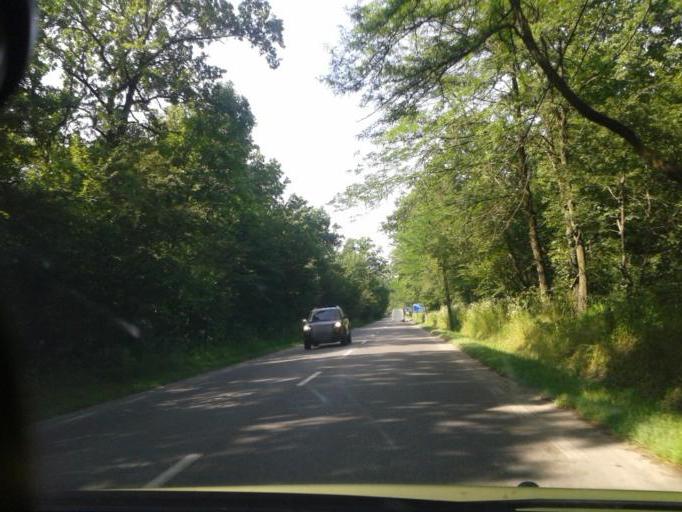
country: RO
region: Prahova
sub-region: Comuna Paulesti
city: Gageni
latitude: 45.0450
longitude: 25.9471
